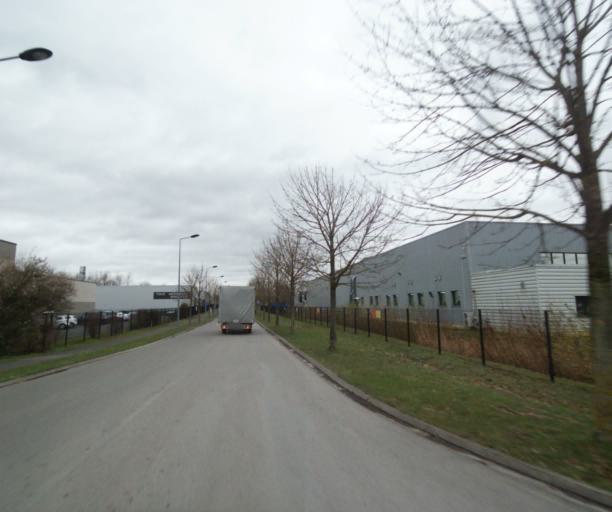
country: FR
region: Nord-Pas-de-Calais
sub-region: Departement du Nord
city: Bruay-sur-l'Escaut
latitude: 50.3938
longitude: 3.5265
